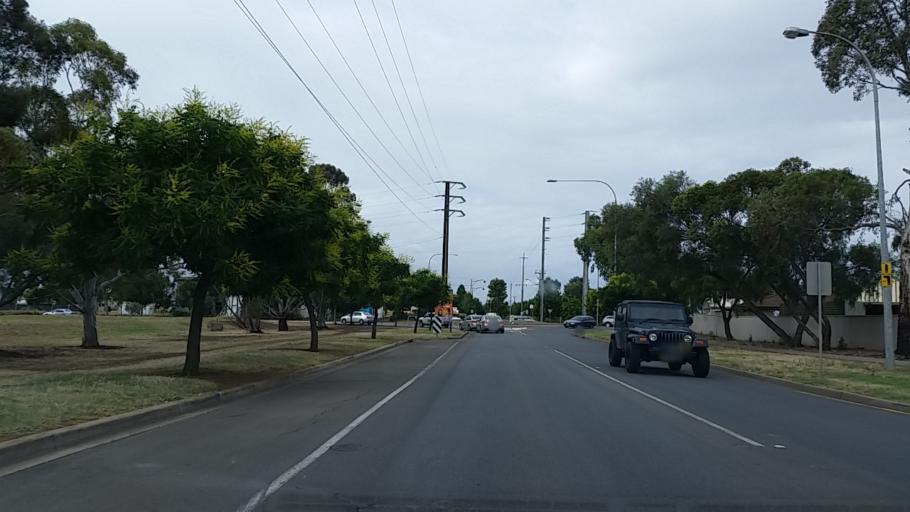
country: AU
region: South Australia
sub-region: Playford
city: Smithfield
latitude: -34.6752
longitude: 138.6842
